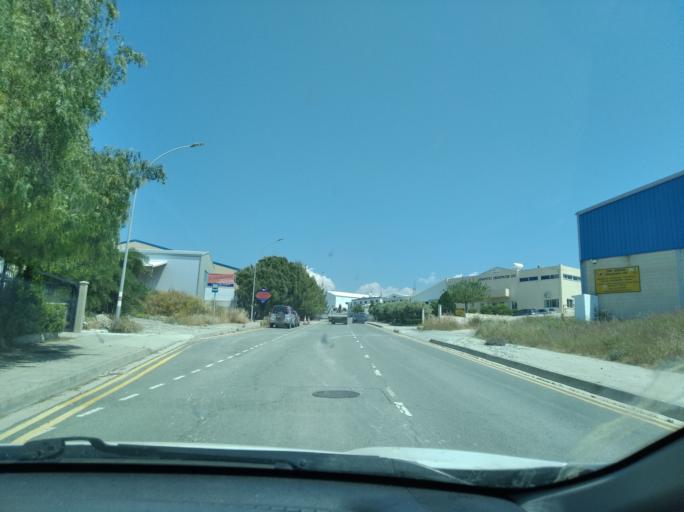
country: CY
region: Limassol
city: Ypsonas
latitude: 34.7292
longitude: 32.9430
